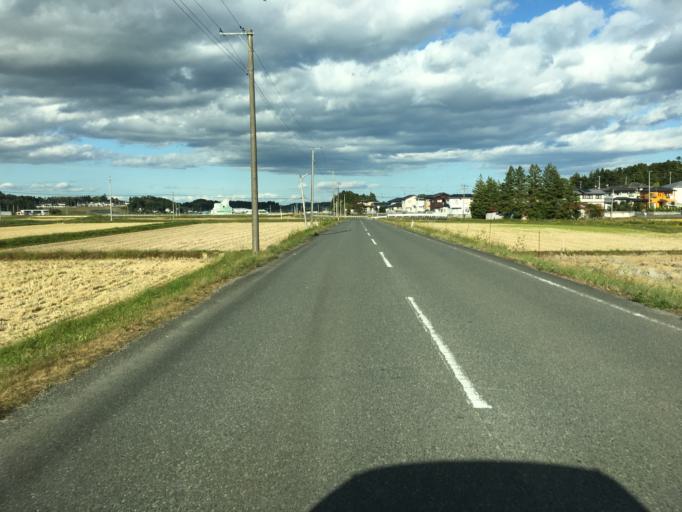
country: JP
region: Miyagi
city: Marumori
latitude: 37.8711
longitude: 140.9085
